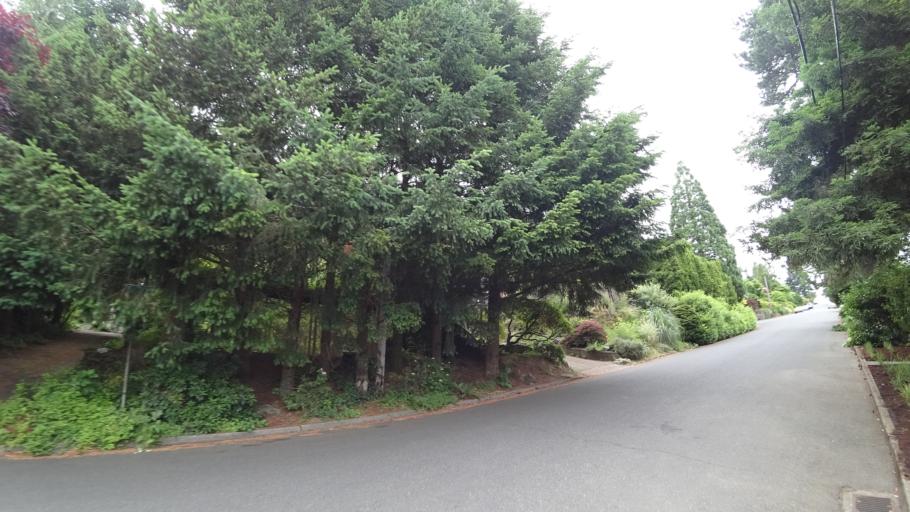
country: US
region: Oregon
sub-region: Multnomah County
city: Lents
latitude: 45.5097
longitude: -122.5889
